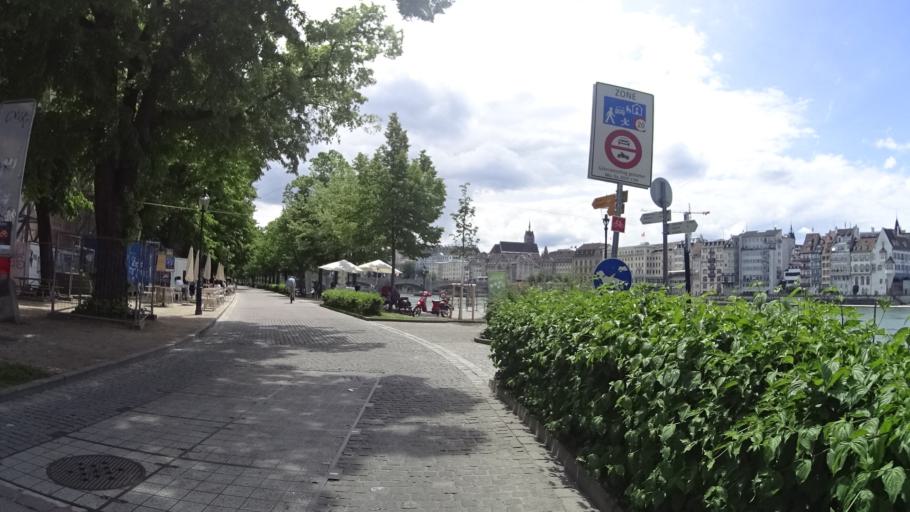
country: CH
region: Basel-City
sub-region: Basel-Stadt
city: Basel
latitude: 47.5631
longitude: 7.5885
